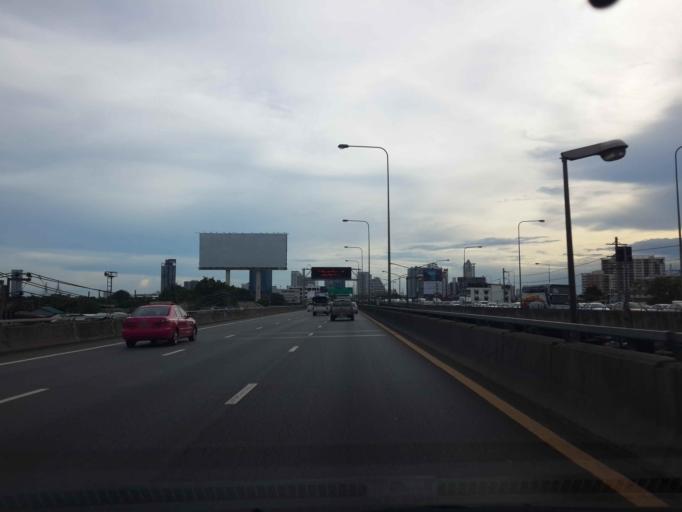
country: TH
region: Bangkok
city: Yan Nawa
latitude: 13.7121
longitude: 100.5530
